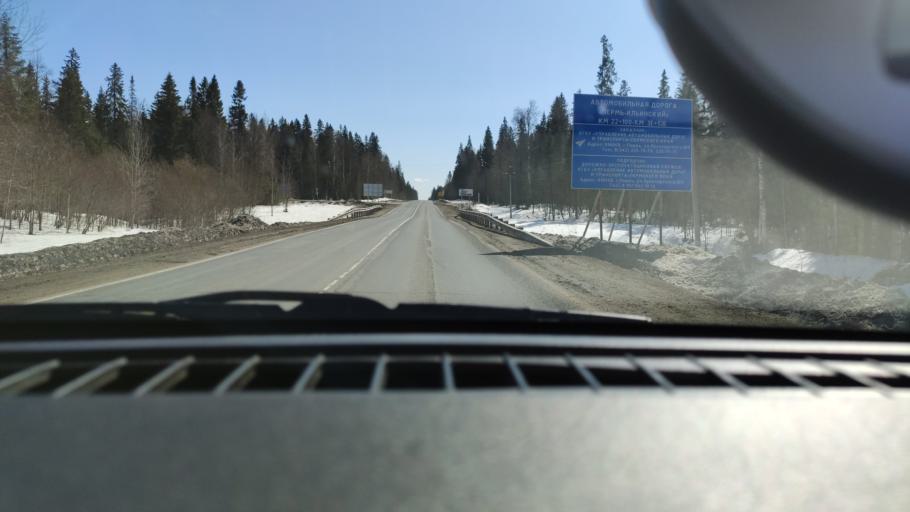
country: RU
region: Perm
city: Perm
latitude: 58.1985
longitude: 56.2076
